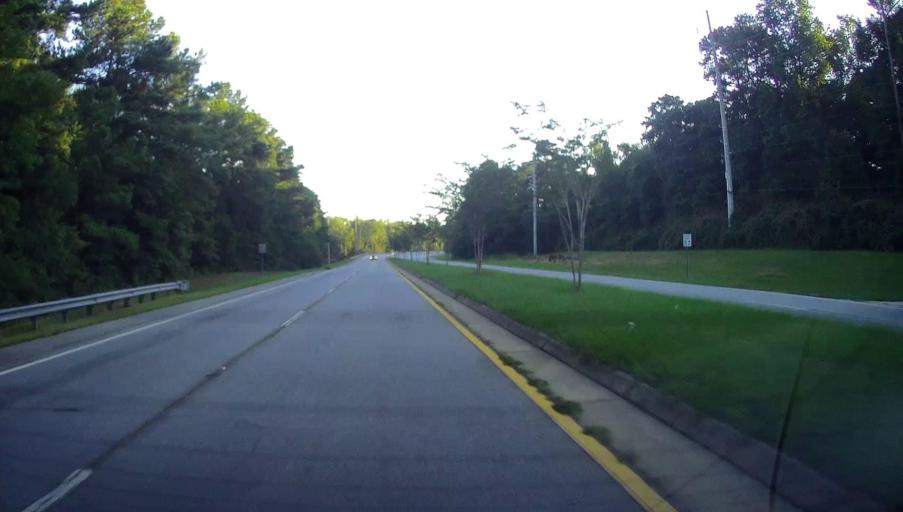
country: US
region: Georgia
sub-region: Muscogee County
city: Columbus
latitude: 32.5313
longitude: -84.8530
